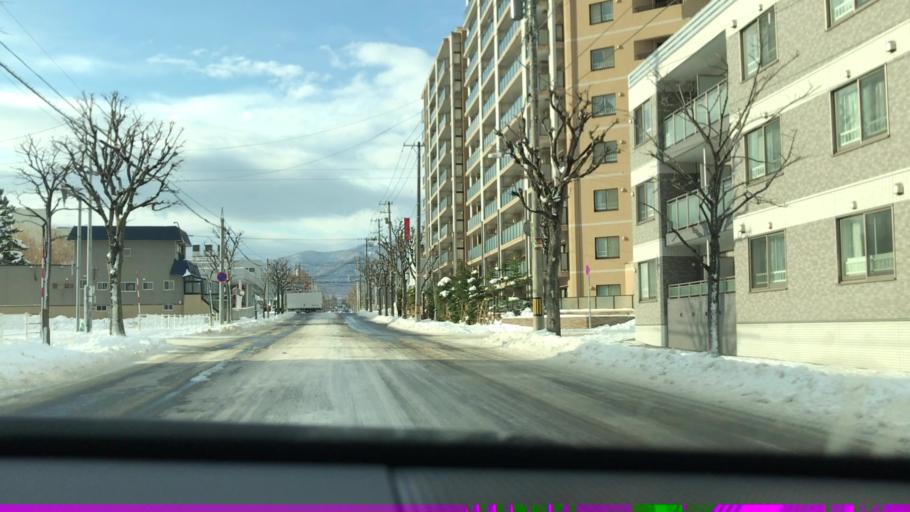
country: JP
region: Hokkaido
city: Sapporo
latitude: 43.0837
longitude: 141.2841
